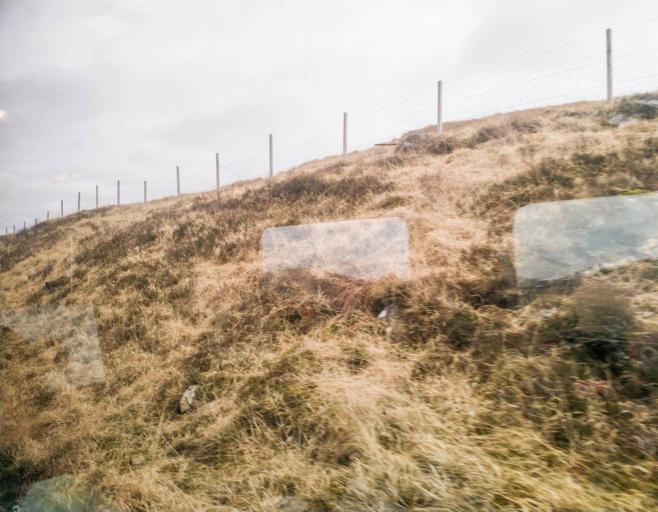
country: GB
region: Scotland
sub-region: Highland
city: Spean Bridge
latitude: 56.5436
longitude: -4.7569
